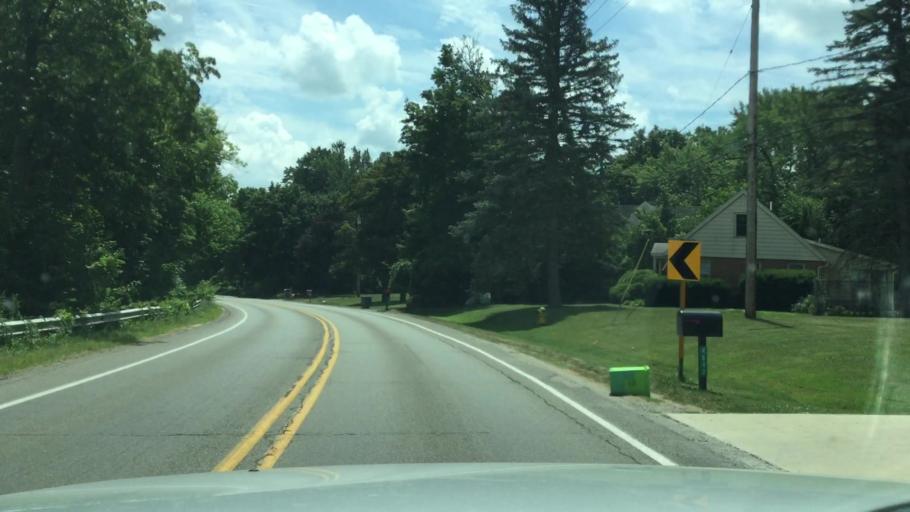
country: US
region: Michigan
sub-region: Genesee County
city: Flushing
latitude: 43.0721
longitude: -83.8727
